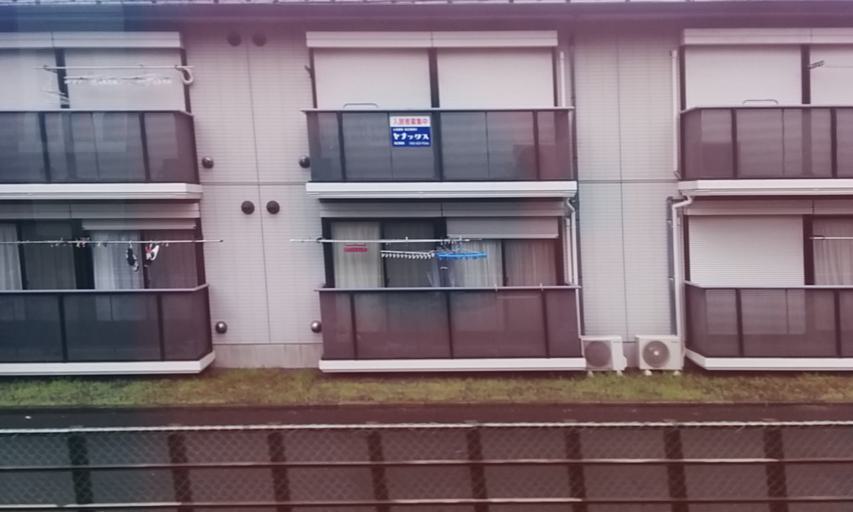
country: JP
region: Tokyo
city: Hino
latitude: 35.6439
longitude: 139.3760
